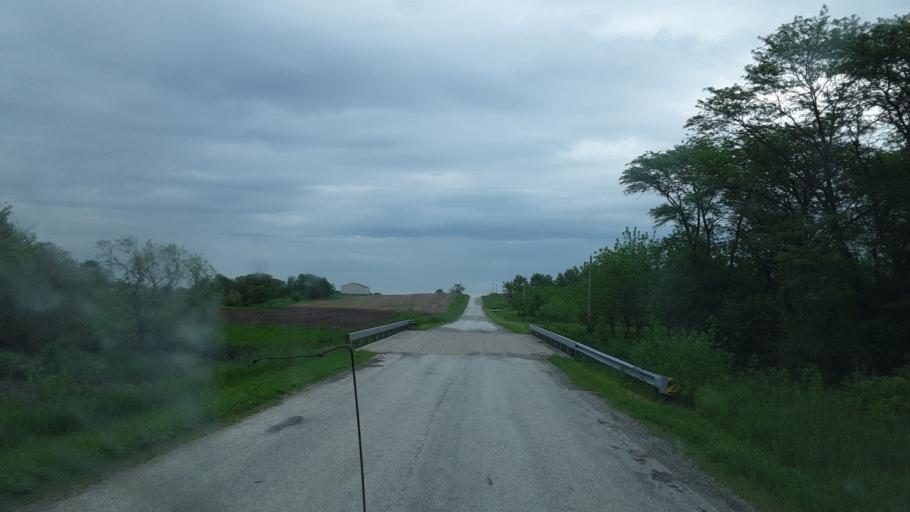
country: US
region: Illinois
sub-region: McDonough County
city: Macomb
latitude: 40.3816
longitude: -90.6083
